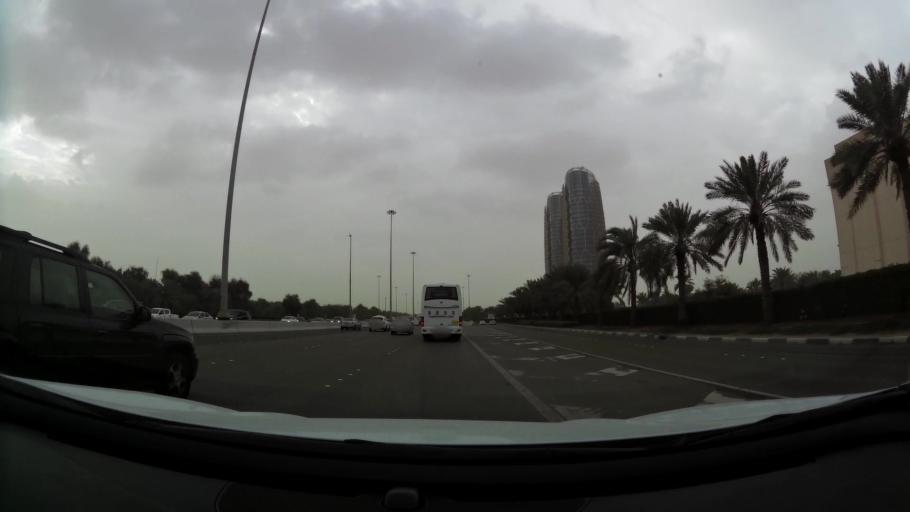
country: AE
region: Abu Dhabi
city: Abu Dhabi
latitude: 24.4602
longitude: 54.3999
